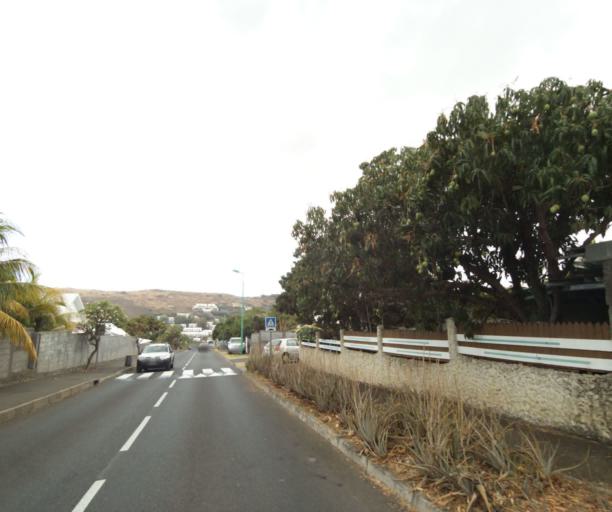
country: RE
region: Reunion
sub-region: Reunion
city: Saint-Paul
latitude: -21.0564
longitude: 55.2279
